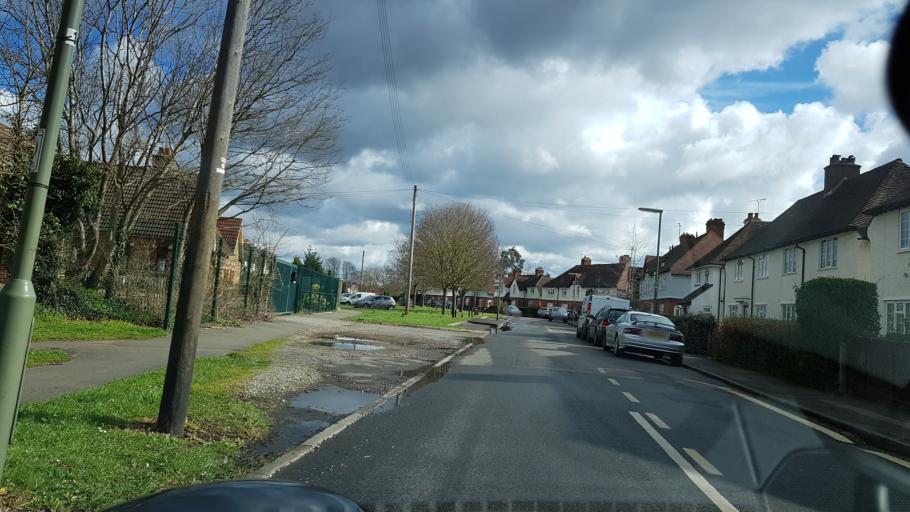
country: GB
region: England
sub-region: Surrey
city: Guildford
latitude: 51.2568
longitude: -0.5732
